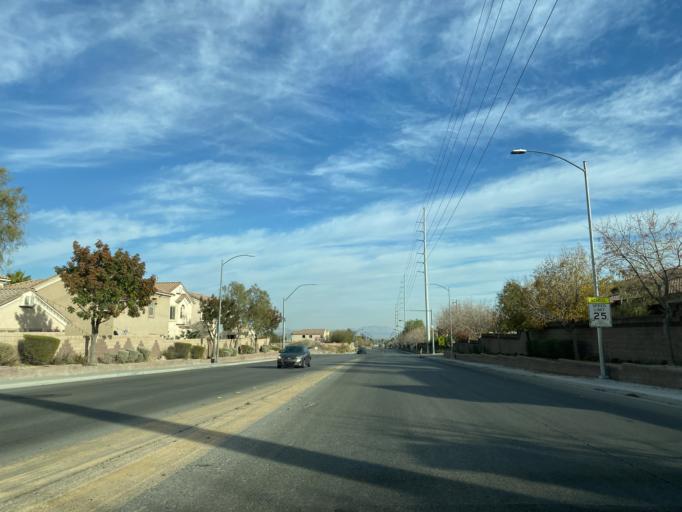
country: US
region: Nevada
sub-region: Clark County
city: Summerlin South
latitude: 36.2993
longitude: -115.3025
